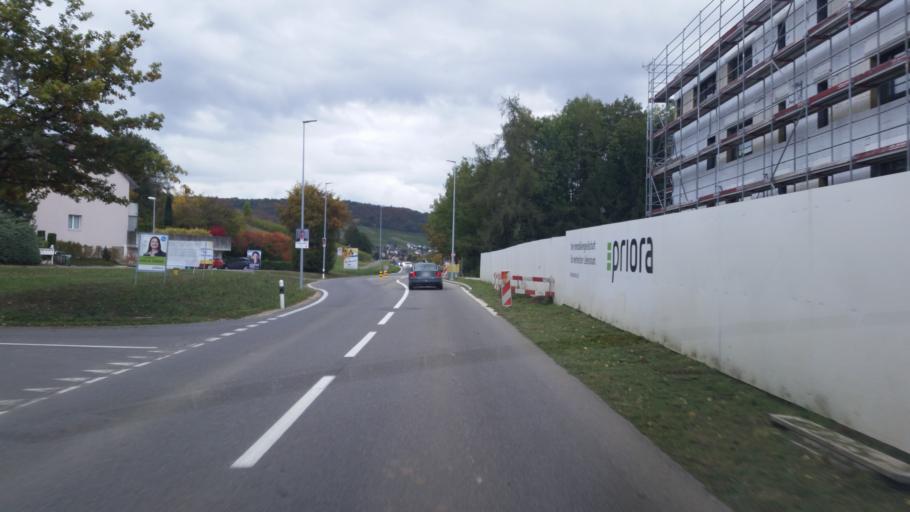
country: CH
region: Aargau
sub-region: Bezirk Zurzach
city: Tegerfelden
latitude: 47.5662
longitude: 8.2688
